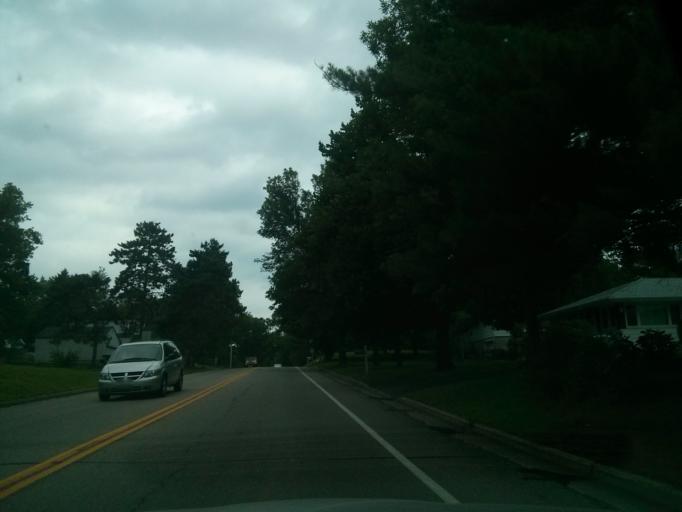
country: US
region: Wisconsin
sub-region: Saint Croix County
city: Hudson
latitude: 44.9707
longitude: -92.7437
